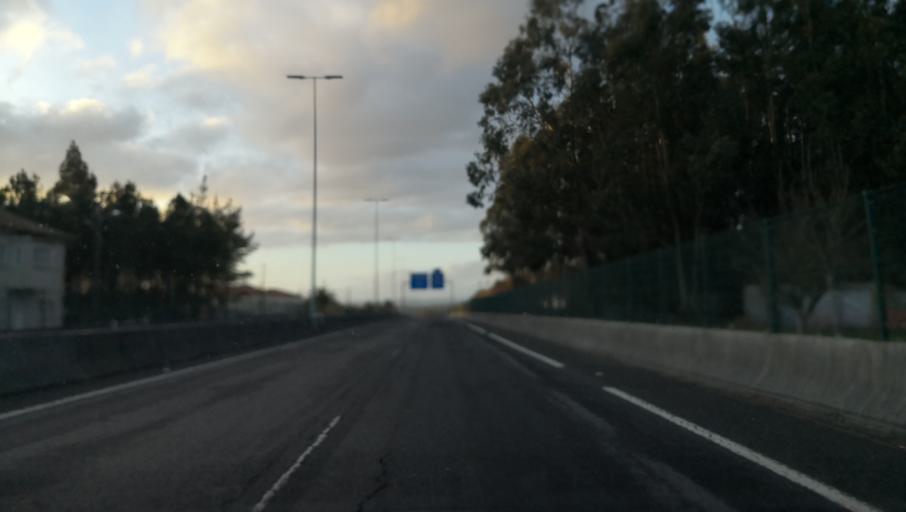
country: ES
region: Galicia
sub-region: Provincia da Coruna
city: Oroso
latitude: 42.9040
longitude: -8.4269
